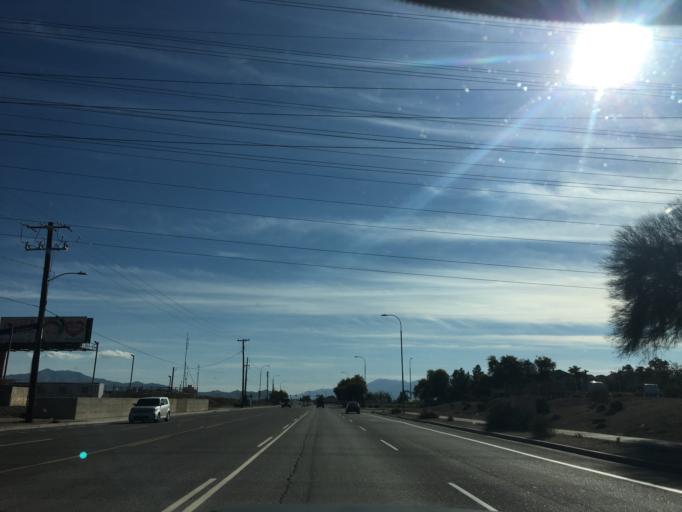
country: US
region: Arizona
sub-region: Maricopa County
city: Laveen
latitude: 33.4160
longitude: -112.1695
